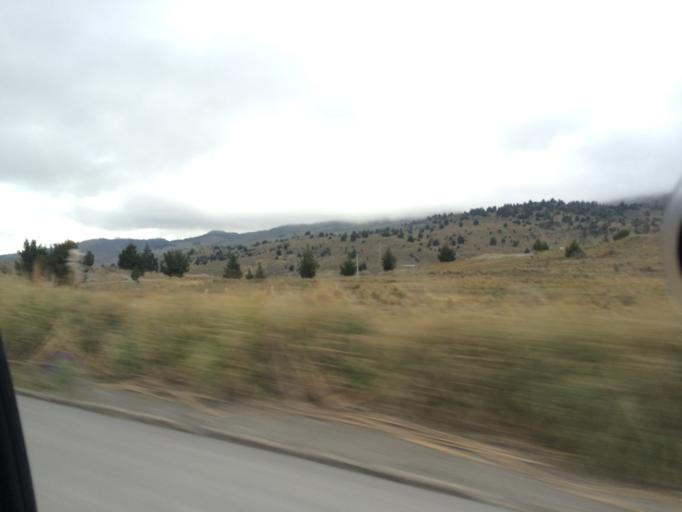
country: EC
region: Chimborazo
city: Alausi
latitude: -2.0026
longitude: -78.7277
